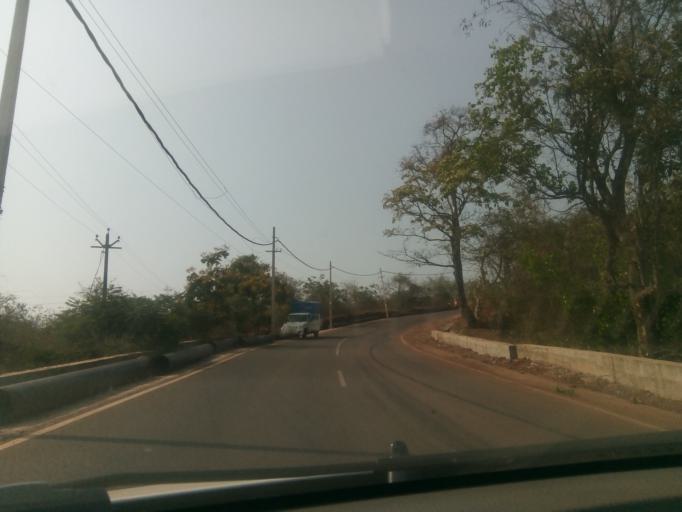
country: IN
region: Goa
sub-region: North Goa
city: Pernem
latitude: 15.7198
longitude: 73.8529
